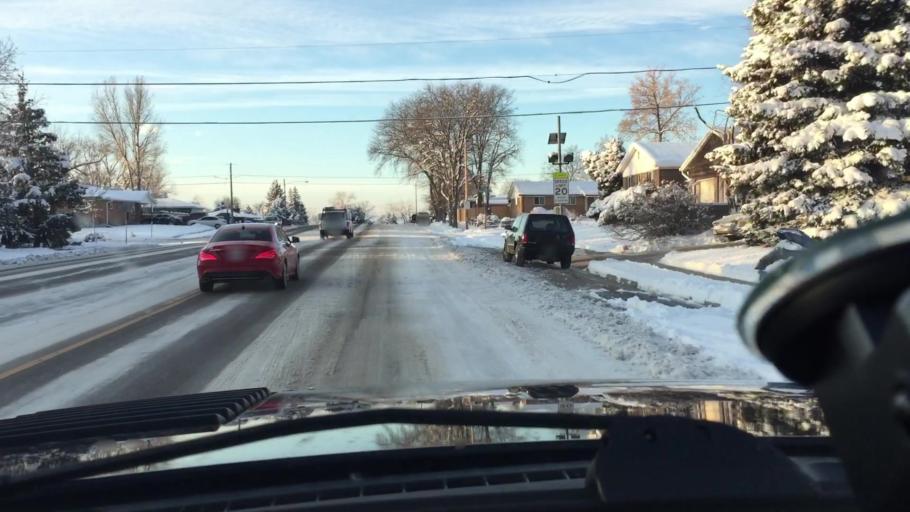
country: US
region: Colorado
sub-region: Adams County
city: Federal Heights
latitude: 39.8452
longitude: -104.9977
